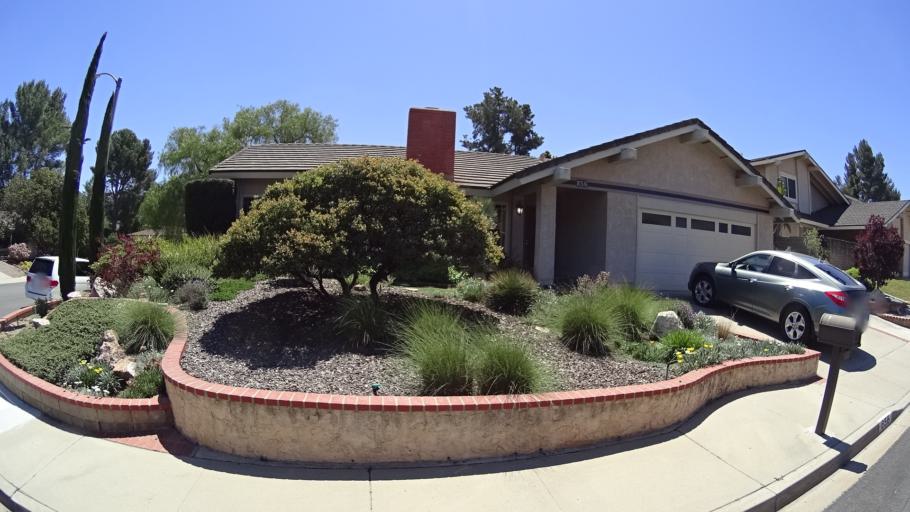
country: US
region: California
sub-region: Ventura County
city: Casa Conejo
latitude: 34.1777
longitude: -118.9011
